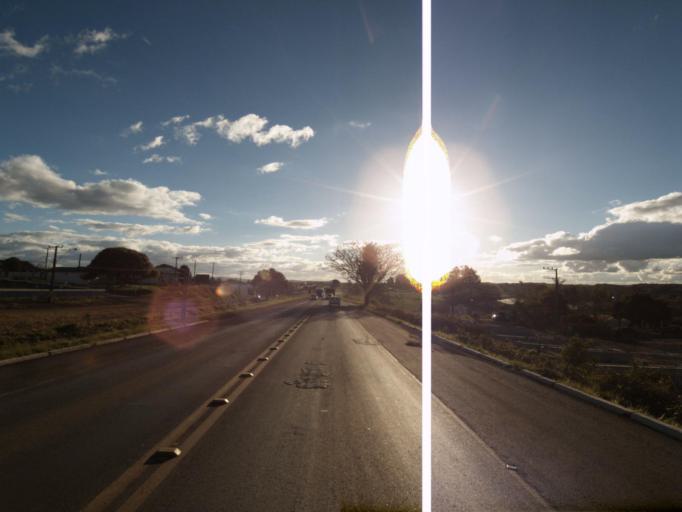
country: BR
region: Santa Catarina
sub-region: Campos Novos
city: Campos Novos
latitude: -27.3887
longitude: -51.2289
